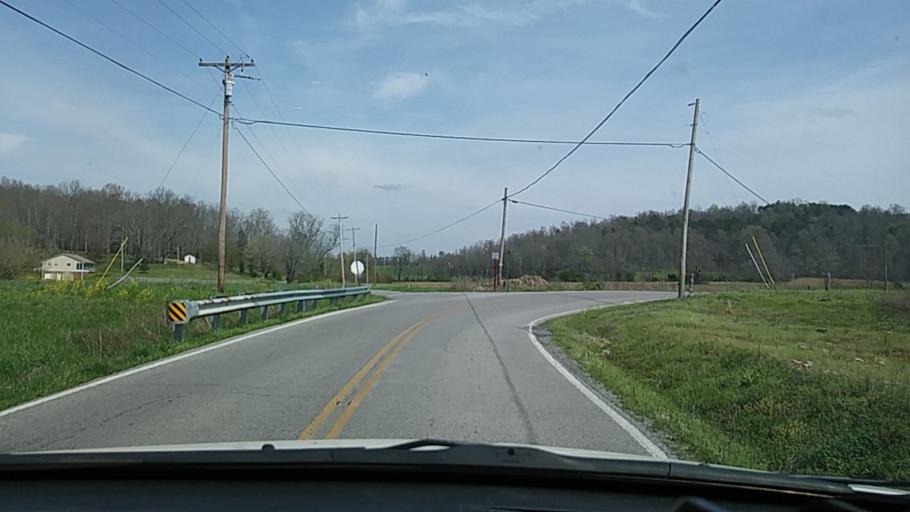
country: US
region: Tennessee
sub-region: Greene County
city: Tusculum
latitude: 36.0999
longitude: -82.7421
